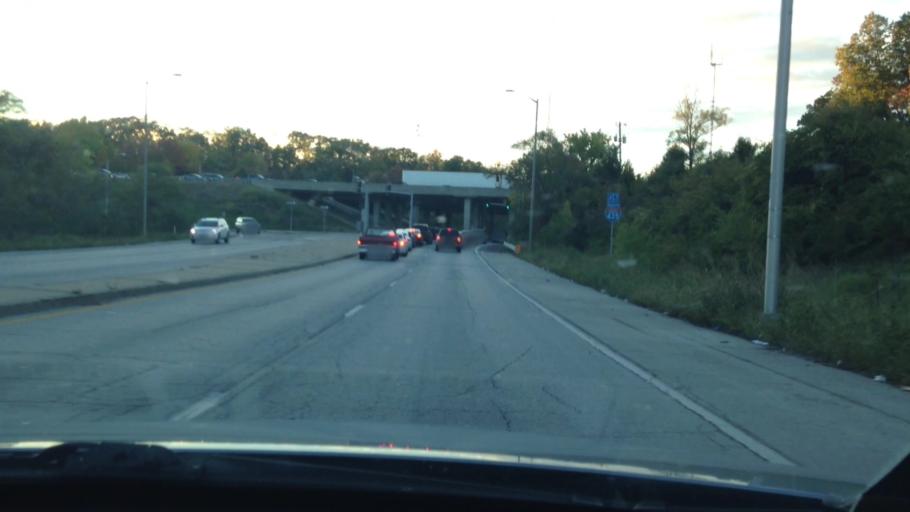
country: US
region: Missouri
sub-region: Jackson County
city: Raytown
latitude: 39.0107
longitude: -94.4964
